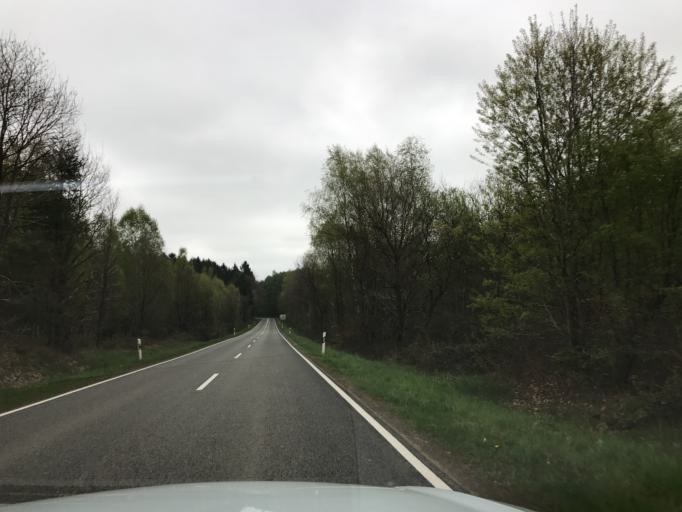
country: DE
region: Saarland
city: Orscholz
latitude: 49.5047
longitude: 6.4934
